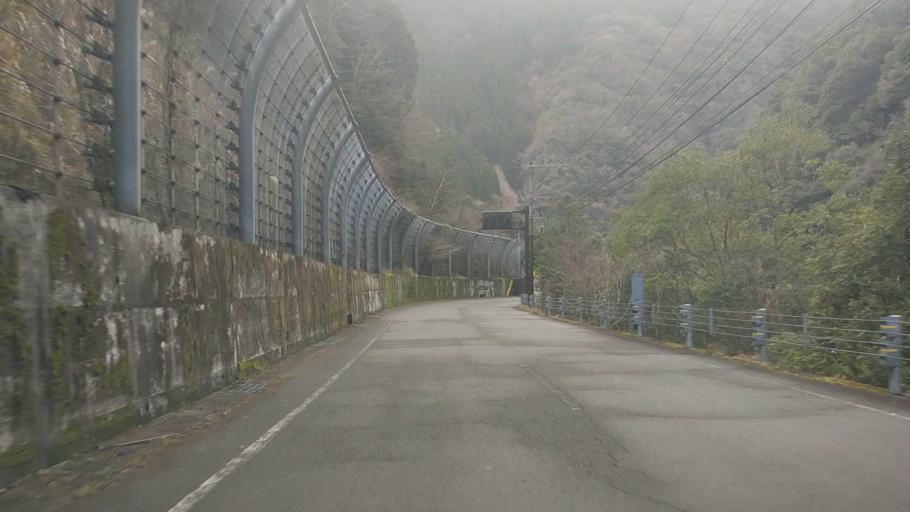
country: JP
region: Kumamoto
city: Matsubase
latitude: 32.4788
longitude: 130.8879
